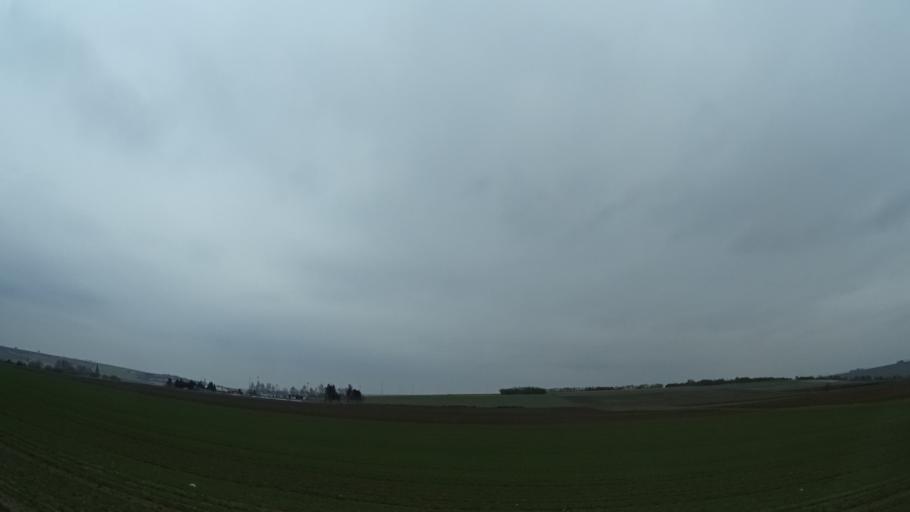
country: DE
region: Rheinland-Pfalz
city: Stetten
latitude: 49.6721
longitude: 8.0806
